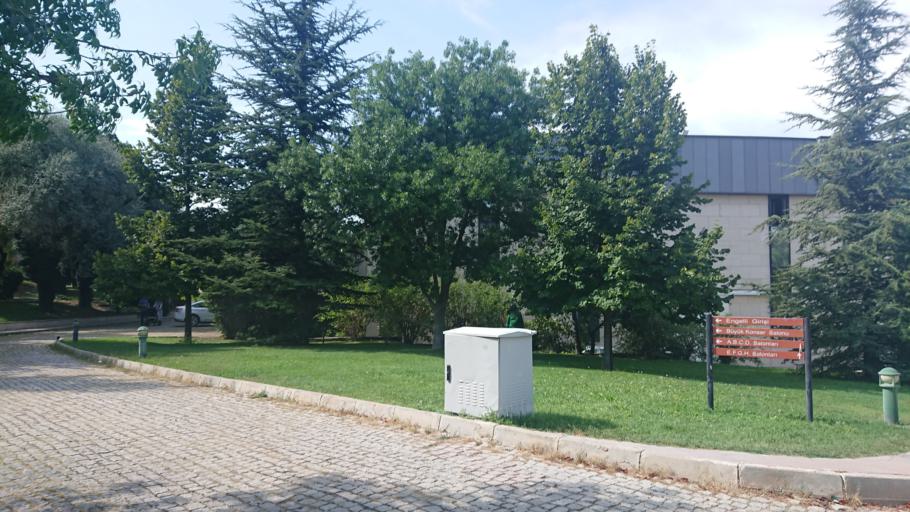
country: TR
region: Ankara
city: Ankara
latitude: 39.8934
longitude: 32.7868
